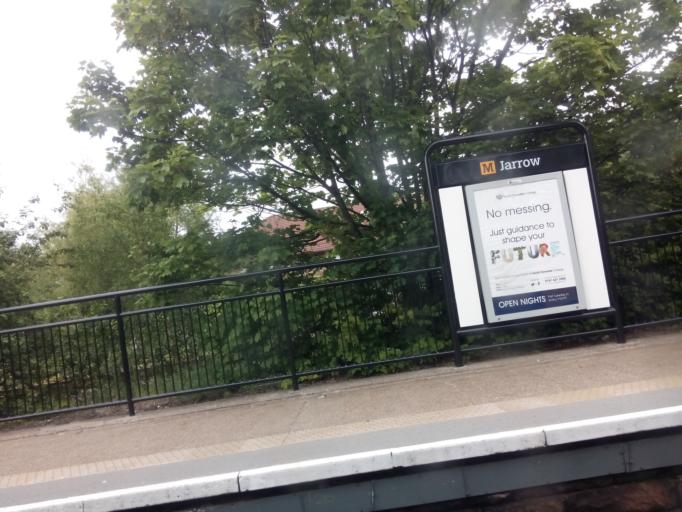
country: GB
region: England
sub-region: South Tyneside
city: Jarrow
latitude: 54.9809
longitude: -1.4956
